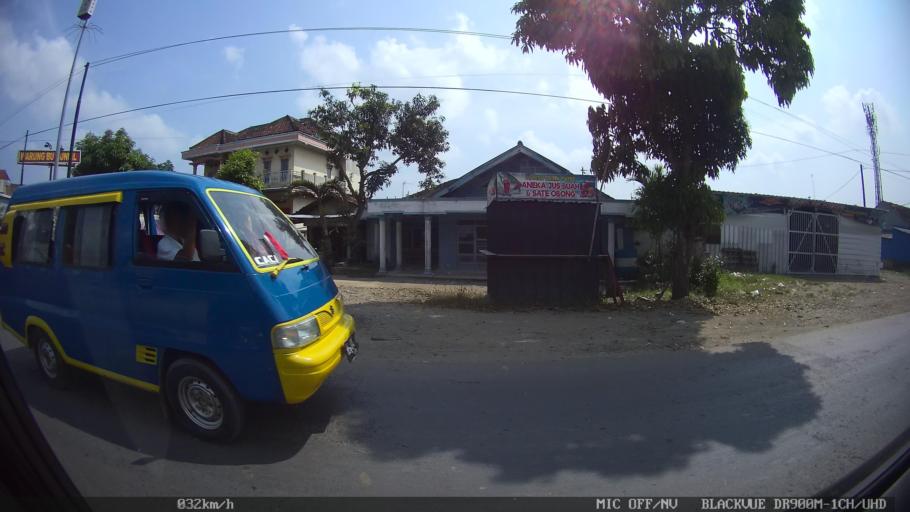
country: ID
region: Lampung
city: Pringsewu
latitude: -5.3622
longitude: 104.9983
